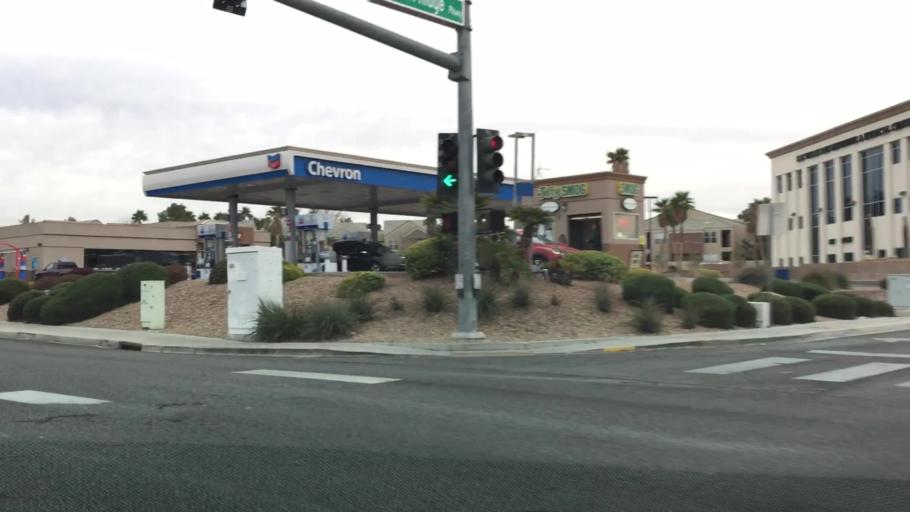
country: US
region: Nevada
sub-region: Clark County
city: Whitney
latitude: 35.9991
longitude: -115.1047
